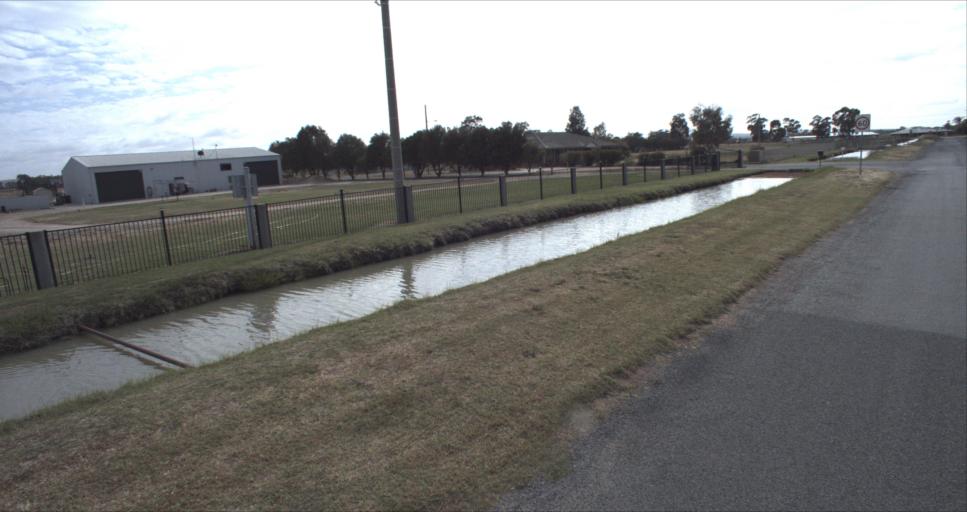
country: AU
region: New South Wales
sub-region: Leeton
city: Leeton
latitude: -34.5577
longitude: 146.4224
